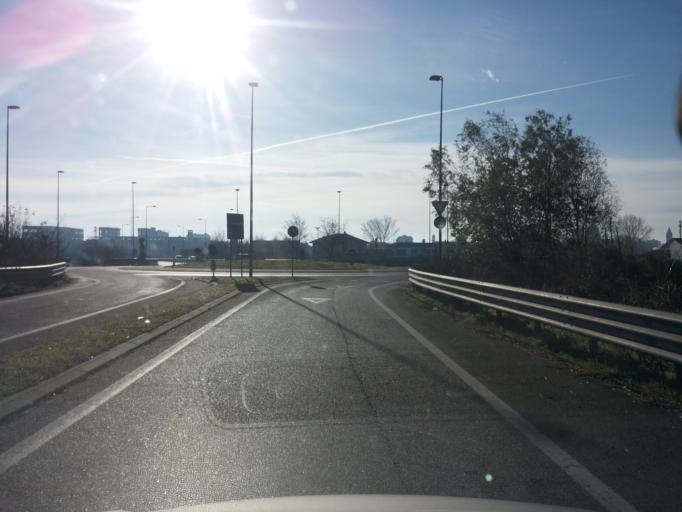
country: IT
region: Piedmont
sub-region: Provincia di Vercelli
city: Vercelli
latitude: 45.3379
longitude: 8.4288
